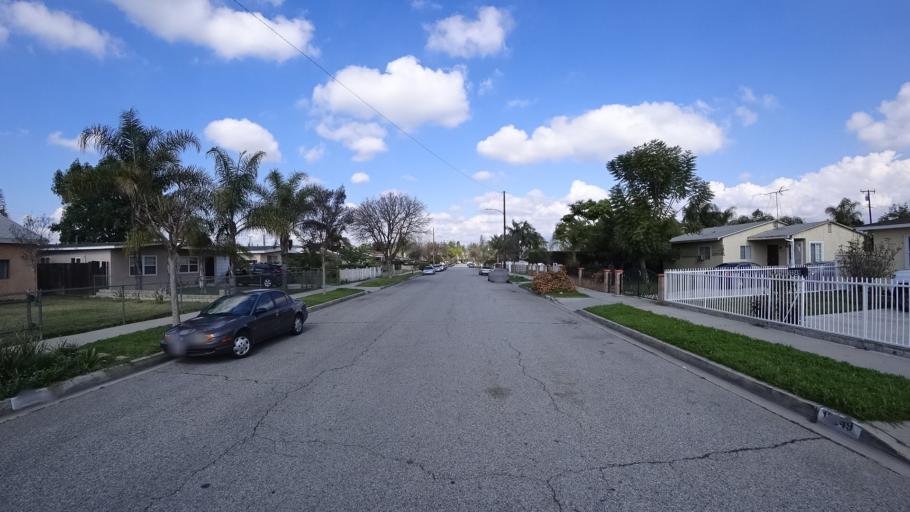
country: US
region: California
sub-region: Los Angeles County
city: Baldwin Park
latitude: 34.0779
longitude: -117.9845
